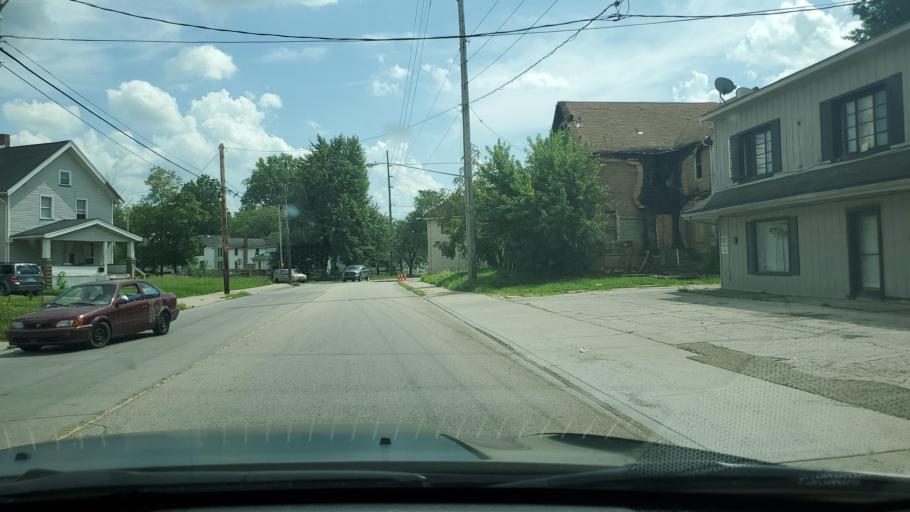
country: US
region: Ohio
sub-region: Trumbull County
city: Warren
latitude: 41.2405
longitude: -80.8360
